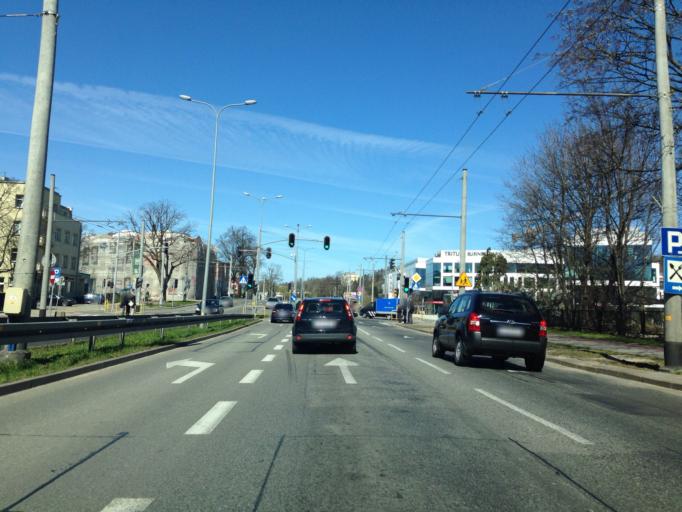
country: PL
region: Pomeranian Voivodeship
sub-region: Sopot
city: Sopot
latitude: 54.4788
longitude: 18.5529
